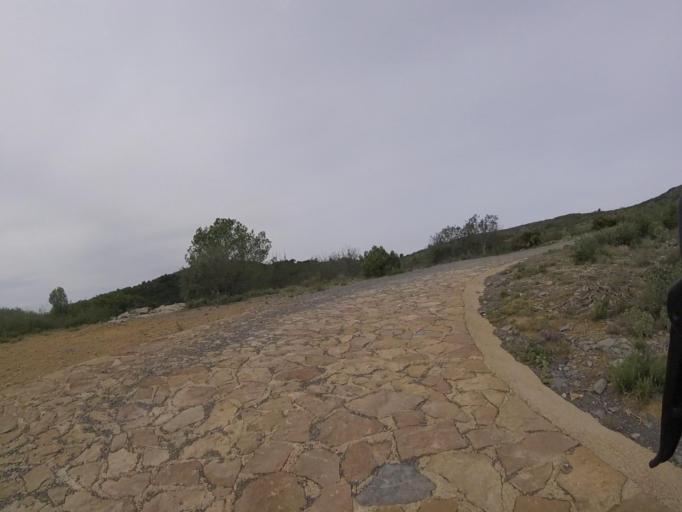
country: ES
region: Valencia
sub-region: Provincia de Castello
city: Benicassim
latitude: 40.0931
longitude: 0.0437
